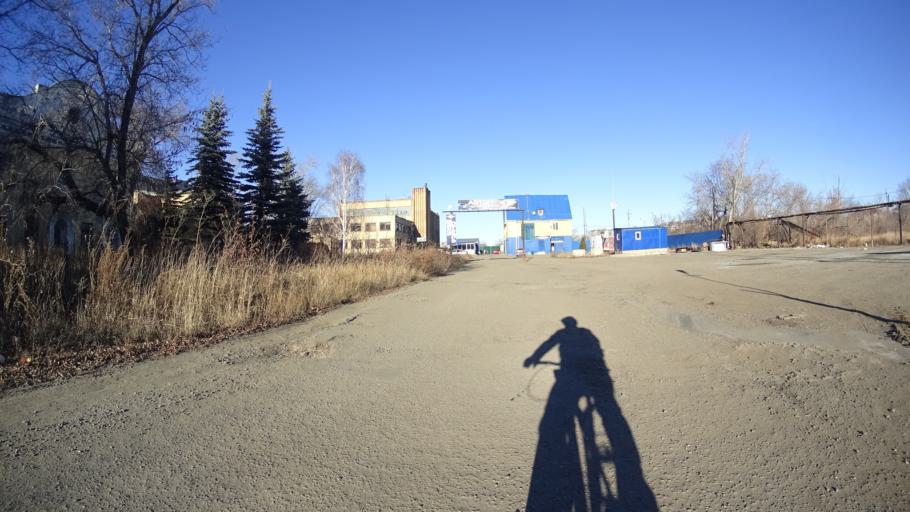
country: RU
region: Chelyabinsk
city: Troitsk
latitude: 54.1023
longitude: 61.5551
